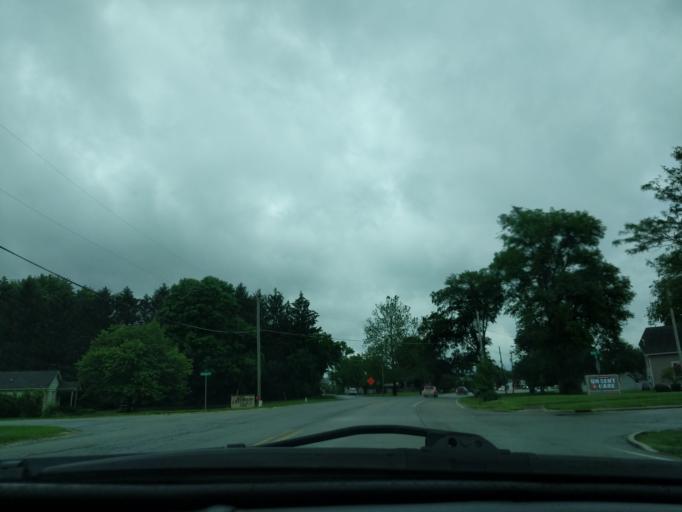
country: US
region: Indiana
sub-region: Hamilton County
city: Noblesville
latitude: 40.0512
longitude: -86.0276
